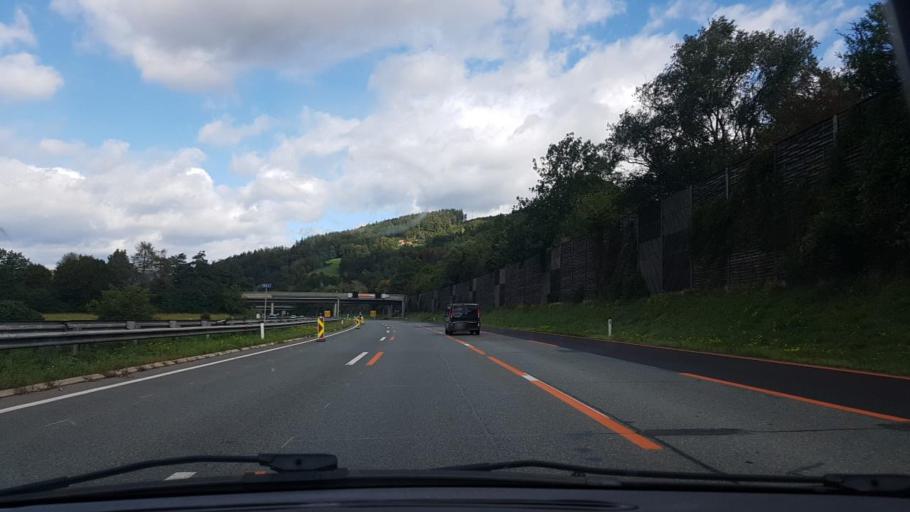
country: AT
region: Styria
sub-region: Politischer Bezirk Graz-Umgebung
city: Deutschfeistritz
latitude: 47.1576
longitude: 15.3300
